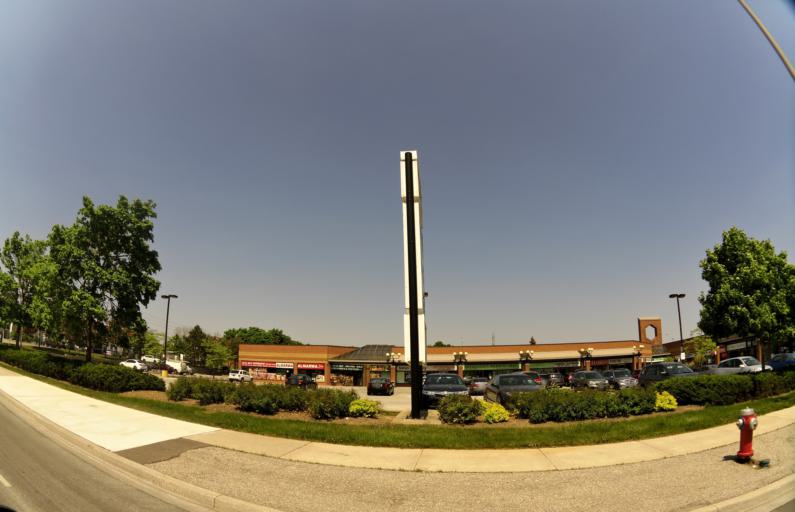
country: CA
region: Ontario
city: Mississauga
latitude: 43.6159
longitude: -79.6413
